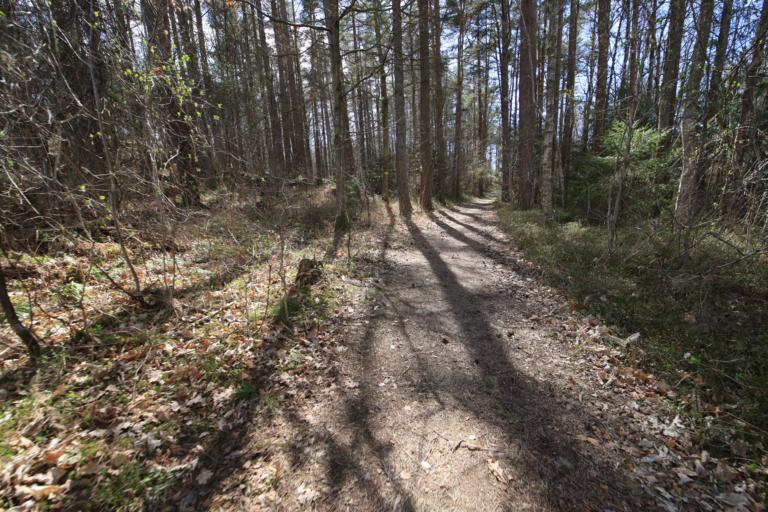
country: SE
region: Halland
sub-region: Varbergs Kommun
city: Varberg
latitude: 57.1801
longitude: 12.2397
